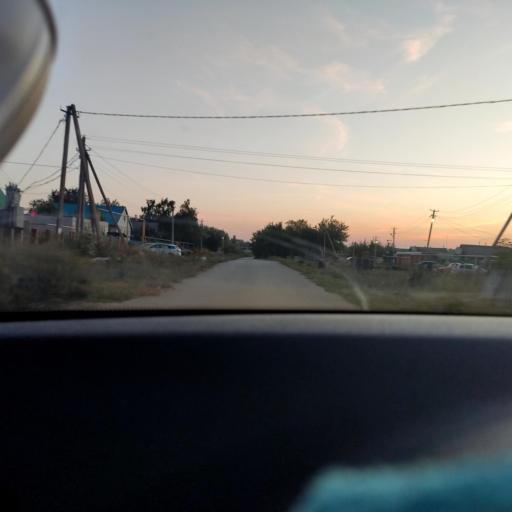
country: RU
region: Samara
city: Novokuybyshevsk
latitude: 53.0766
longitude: 50.0135
